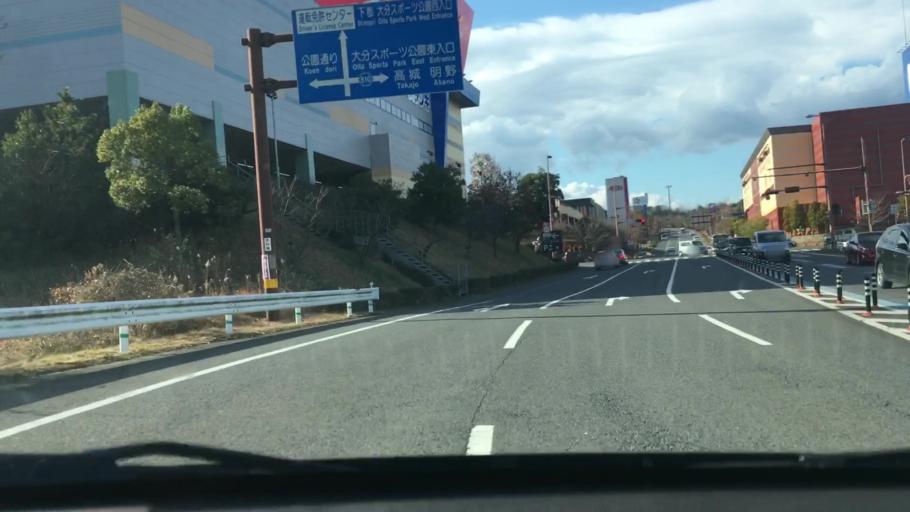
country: JP
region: Oita
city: Tsurusaki
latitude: 33.1953
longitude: 131.6615
